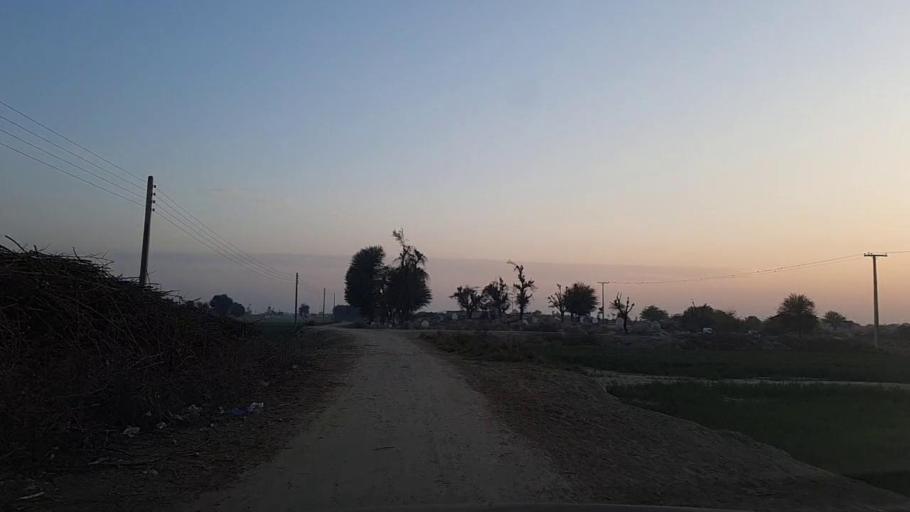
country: PK
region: Sindh
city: Jam Sahib
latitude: 26.4609
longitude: 68.5215
